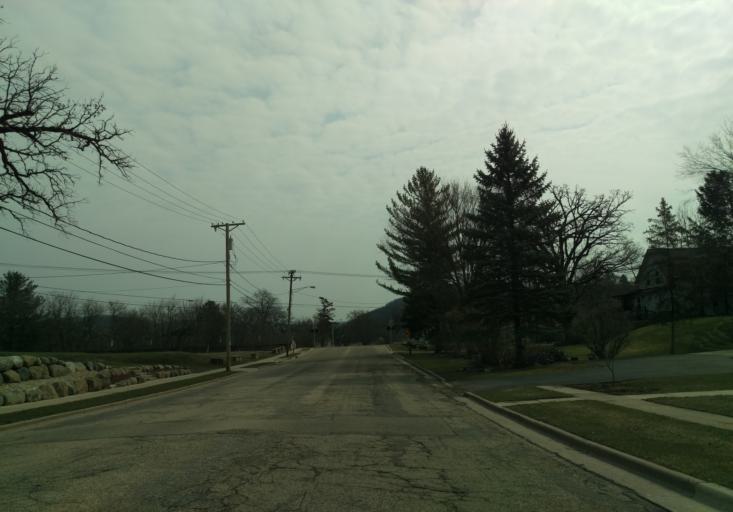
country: US
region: Wisconsin
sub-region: Columbia County
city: Lodi
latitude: 43.3124
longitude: -89.5317
